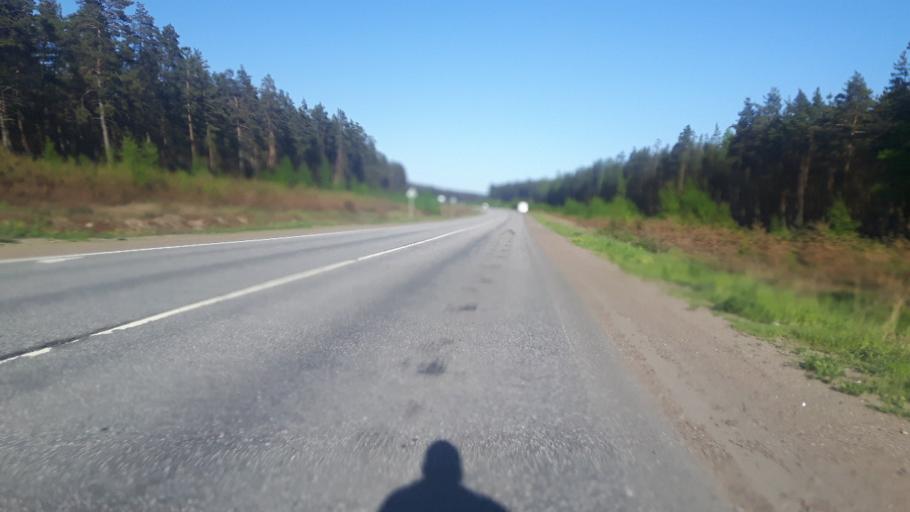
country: RU
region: Leningrad
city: Lebyazh'ye
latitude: 60.1682
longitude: 29.2252
